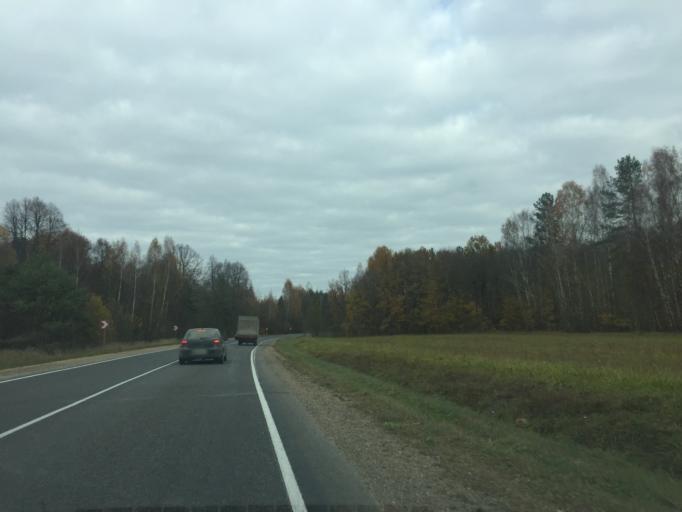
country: BY
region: Minsk
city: Svir
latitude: 54.8423
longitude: 26.2004
